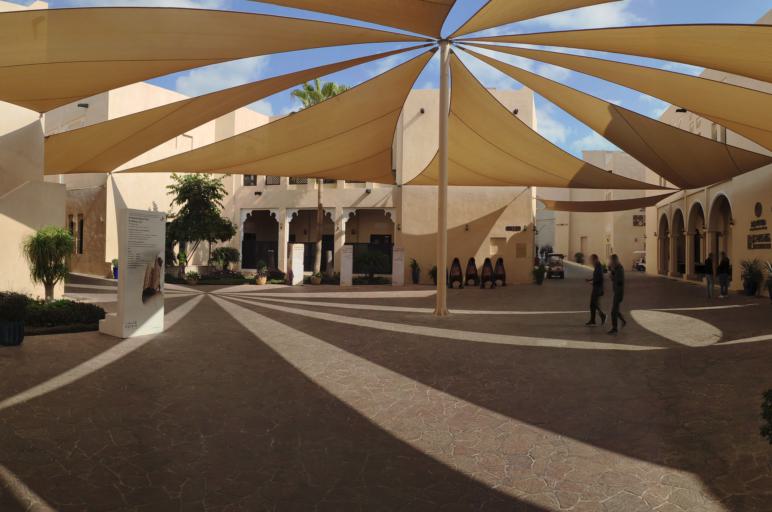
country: QA
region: Baladiyat ad Dawhah
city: Doha
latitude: 25.3598
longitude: 51.5252
